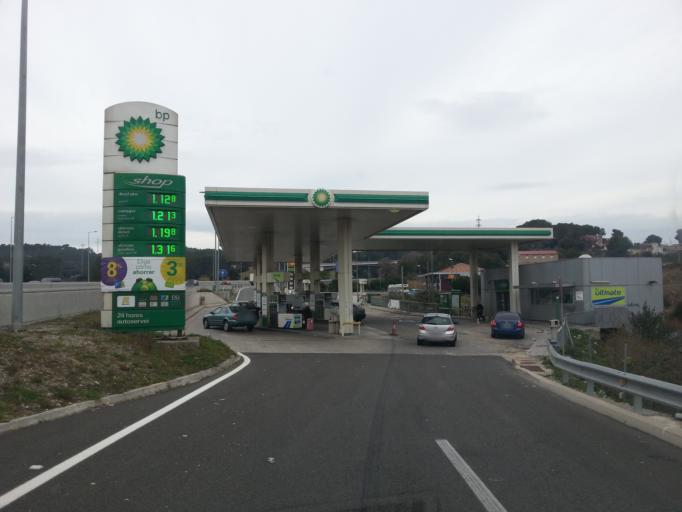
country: ES
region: Catalonia
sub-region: Provincia de Barcelona
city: Montcada i Reixac
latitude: 41.4703
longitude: 2.1664
